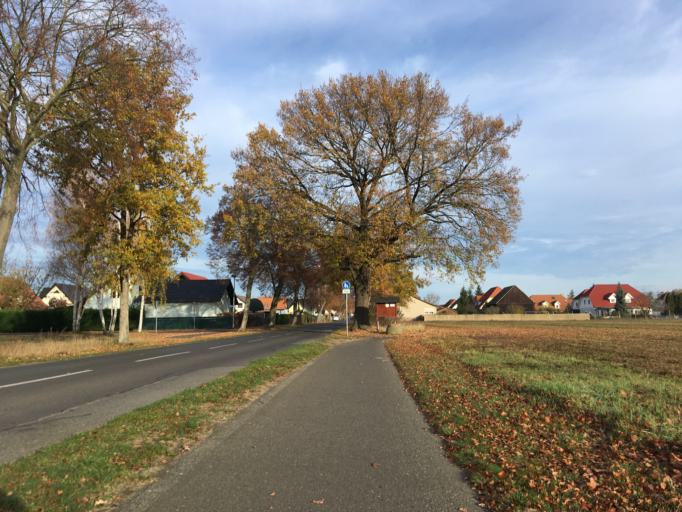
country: DE
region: Brandenburg
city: Luebben
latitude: 51.9652
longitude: 13.8857
